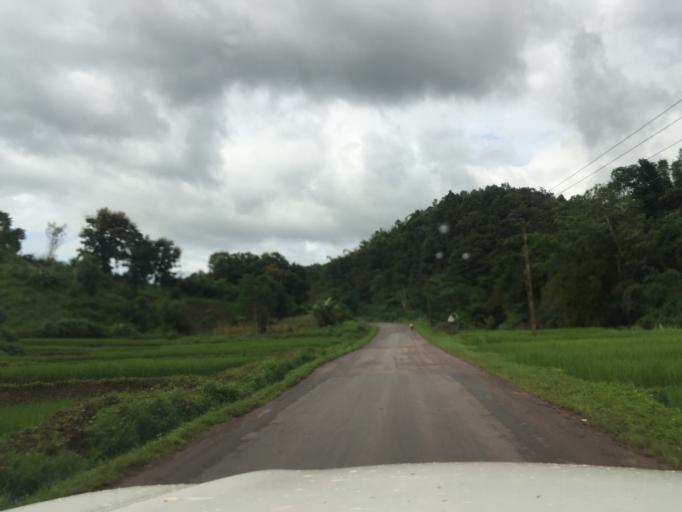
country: LA
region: Oudomxai
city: Muang La
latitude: 20.8087
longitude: 102.0893
